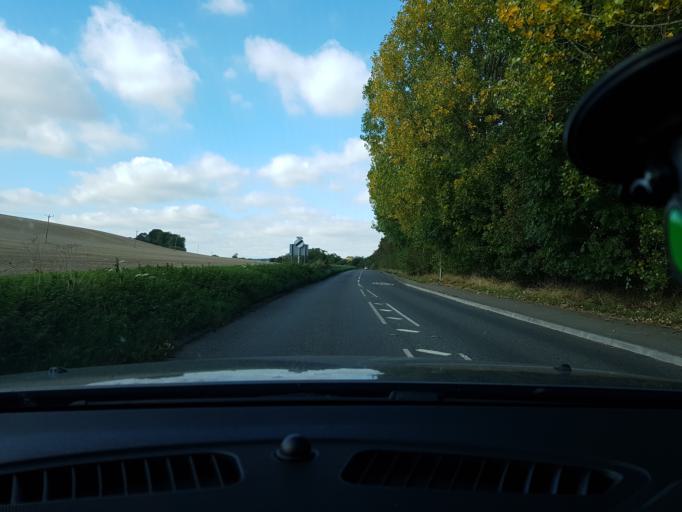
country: GB
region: England
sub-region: West Berkshire
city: Hungerford
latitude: 51.4206
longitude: -1.5200
